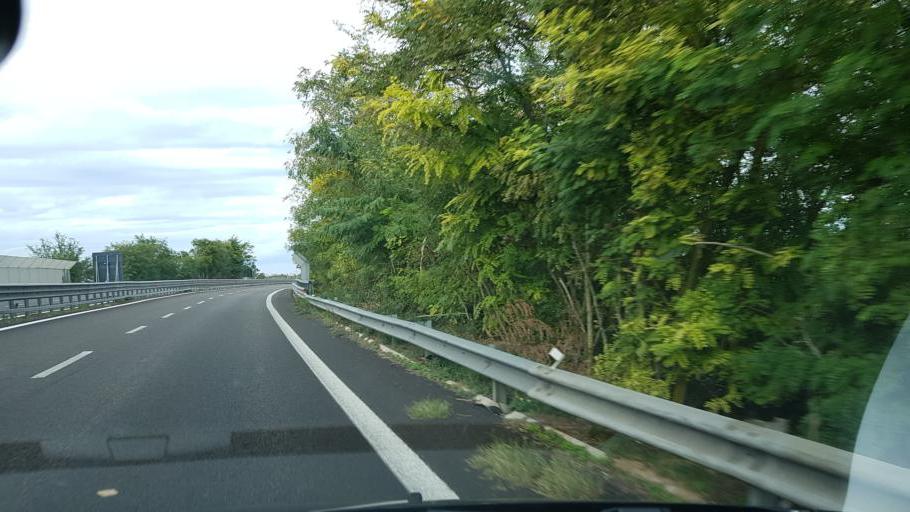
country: IT
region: Apulia
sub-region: Provincia di Lecce
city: Castromediano
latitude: 40.3272
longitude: 18.1856
